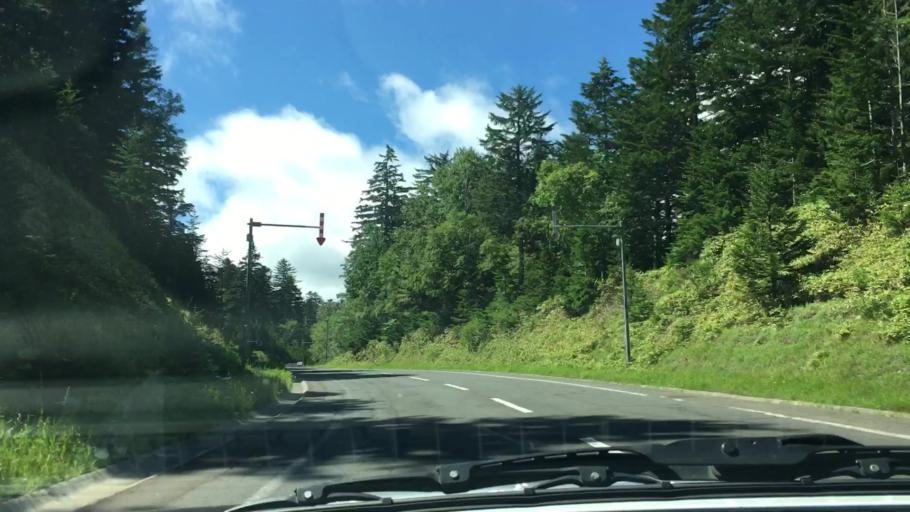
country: JP
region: Hokkaido
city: Kitami
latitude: 43.4385
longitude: 144.0069
